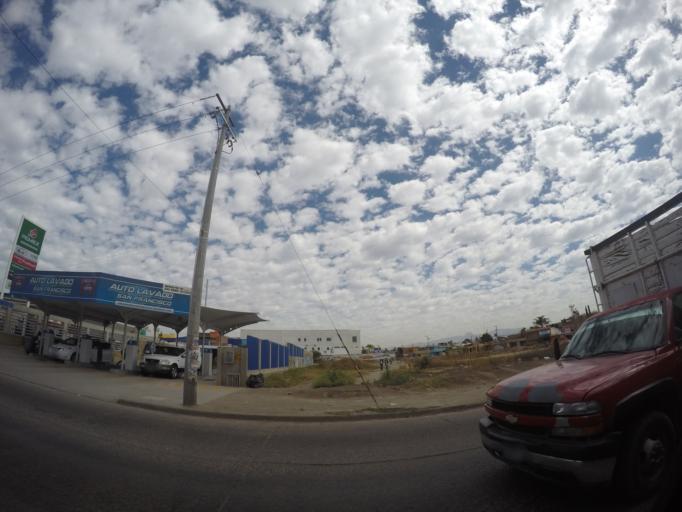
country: MX
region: Guanajuato
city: Leon
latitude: 21.0982
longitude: -101.6668
